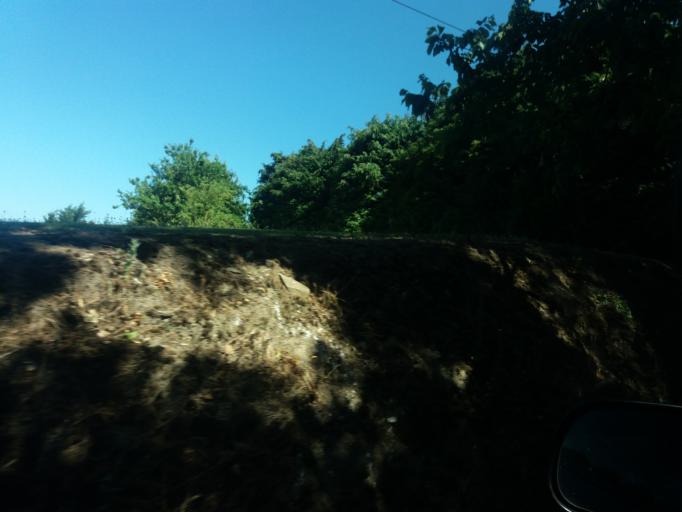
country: IE
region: Leinster
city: Ballymun
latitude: 53.4489
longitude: -6.2886
